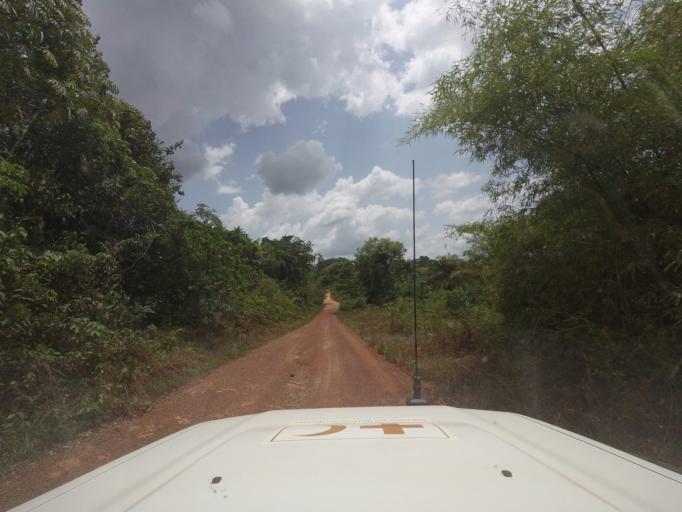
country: LR
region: Bong
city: Gbarnga
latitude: 7.0593
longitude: -9.2381
